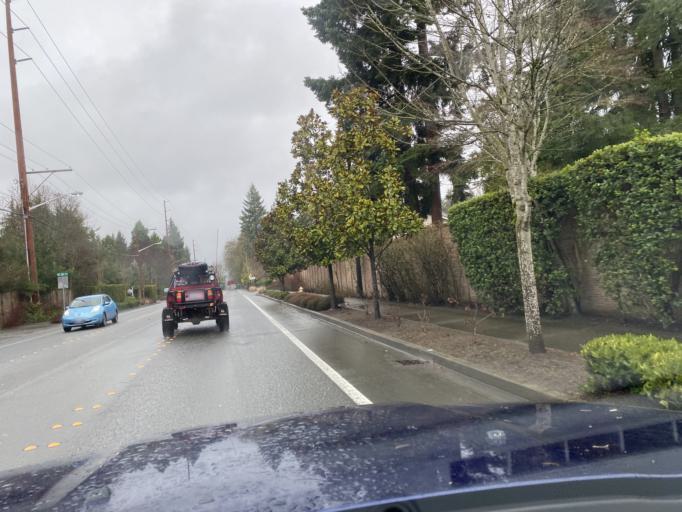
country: US
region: Washington
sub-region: King County
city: Eastgate
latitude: 47.6123
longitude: -122.1535
